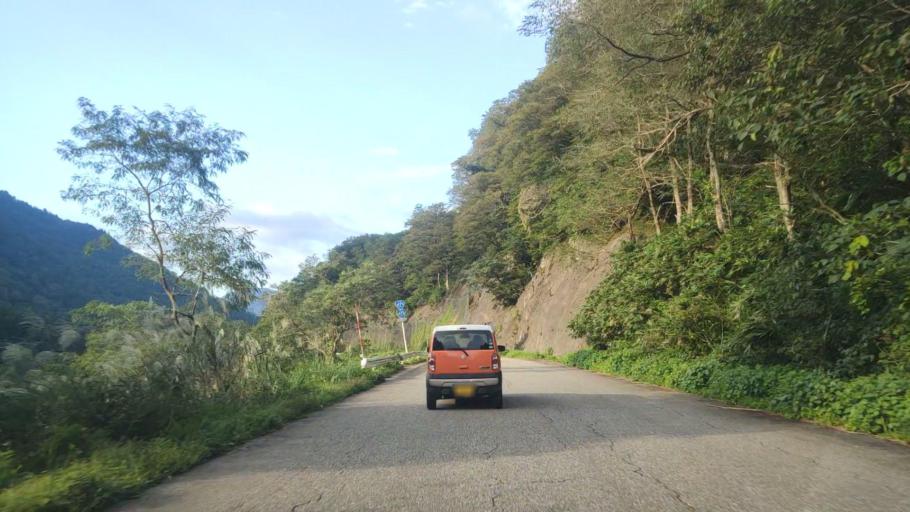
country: JP
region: Toyama
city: Yatsuomachi-higashikumisaka
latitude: 36.4508
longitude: 137.0848
